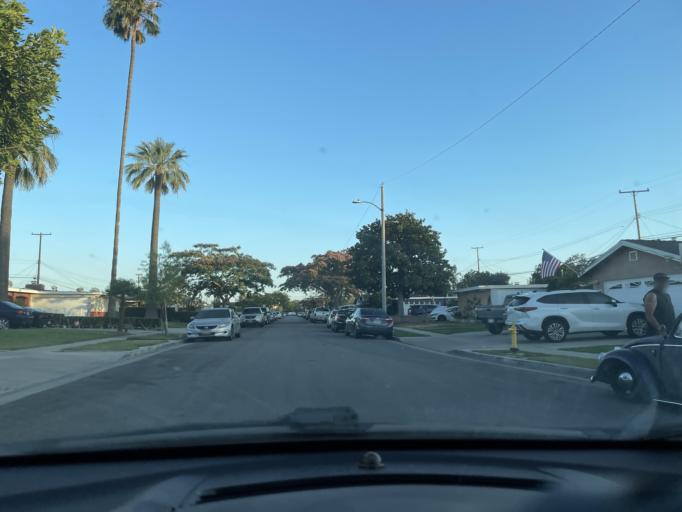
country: US
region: California
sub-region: Los Angeles County
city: La Mirada
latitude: 33.9132
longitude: -118.0324
